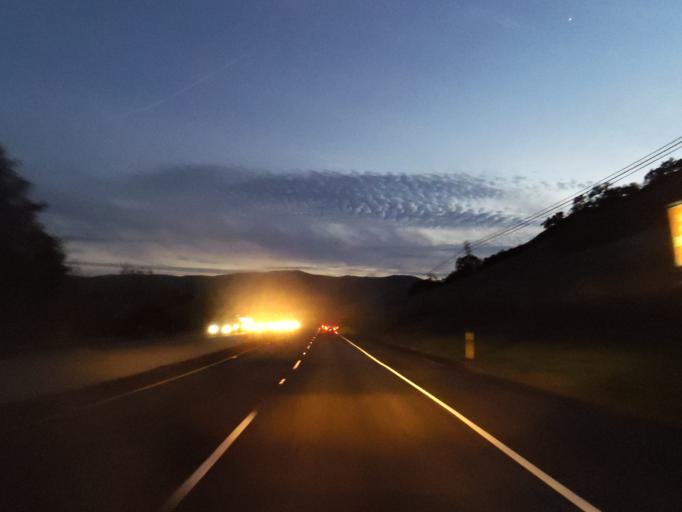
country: US
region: California
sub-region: San Luis Obispo County
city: San Luis Obispo
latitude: 35.3123
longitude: -120.6243
